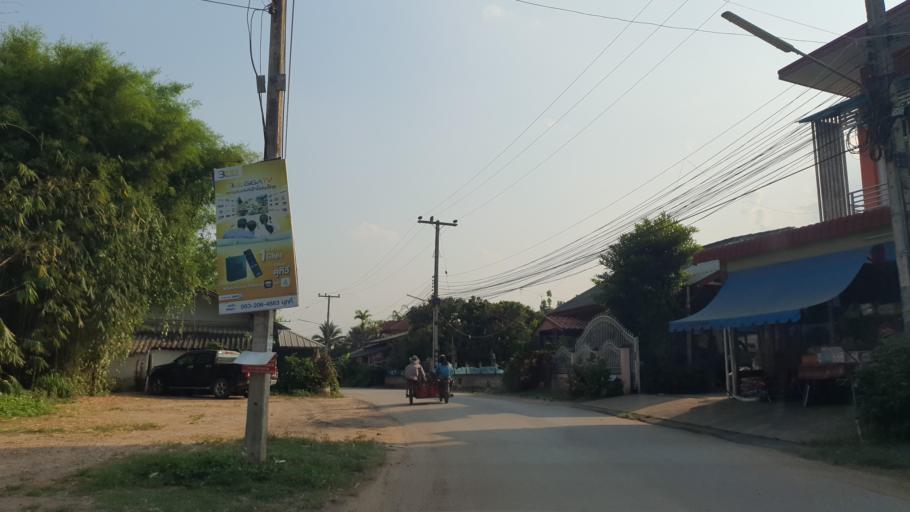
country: TH
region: Chiang Mai
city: Mae Wang
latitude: 18.6631
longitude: 98.8193
